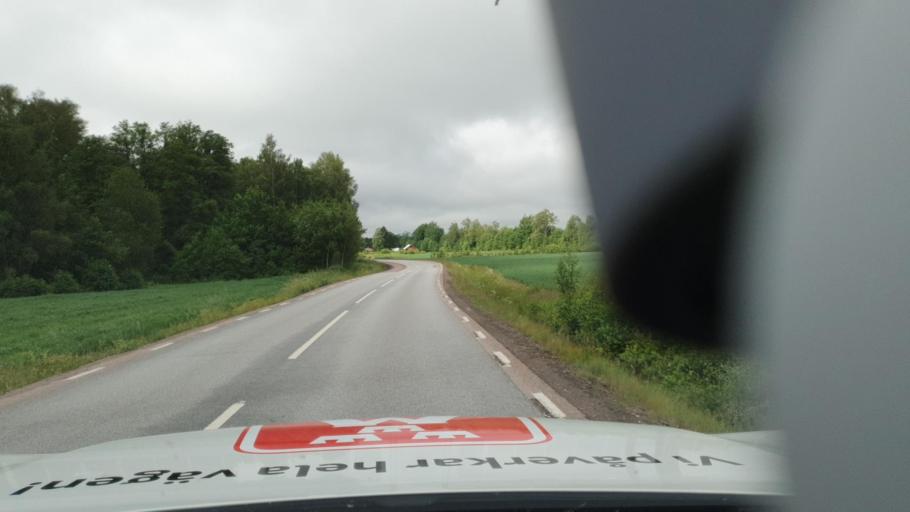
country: SE
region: Vaermland
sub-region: Kristinehamns Kommun
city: Bjorneborg
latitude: 59.1183
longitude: 14.1935
